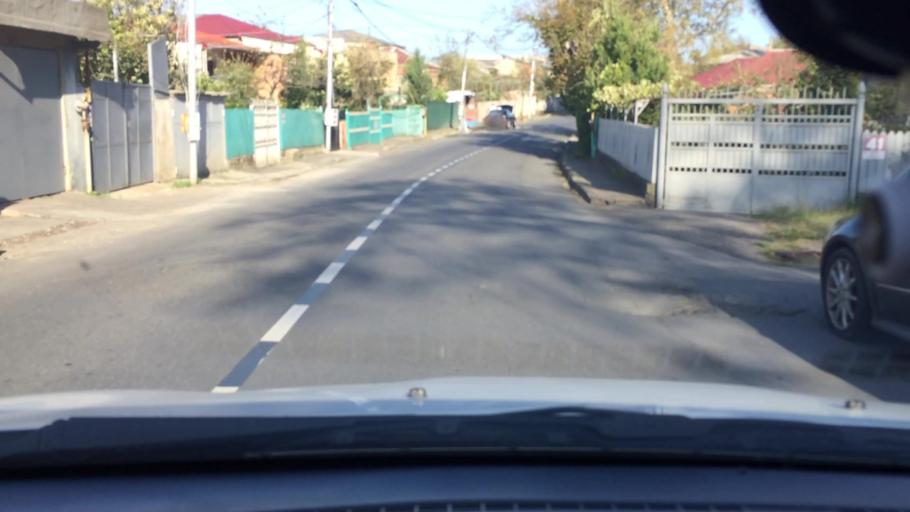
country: GE
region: Imereti
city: Kutaisi
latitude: 42.2695
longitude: 42.7145
